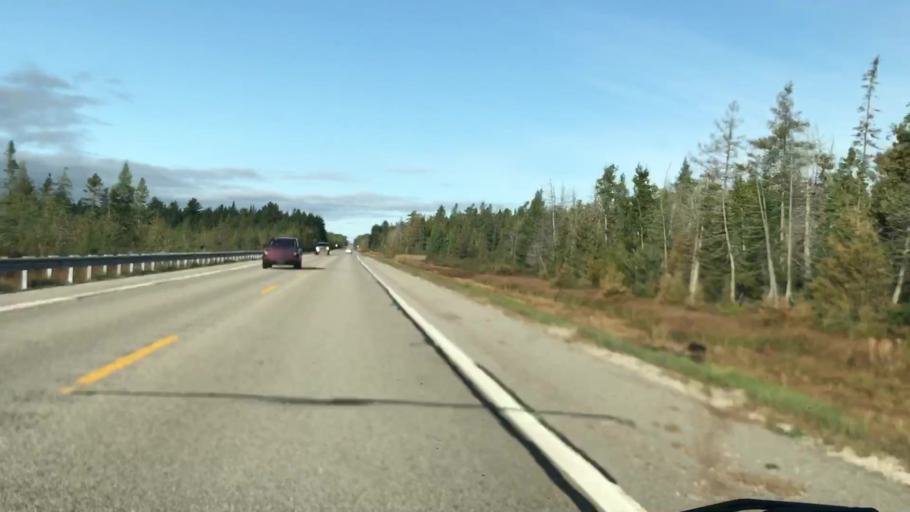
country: US
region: Michigan
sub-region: Luce County
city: Newberry
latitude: 46.3036
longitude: -85.3263
